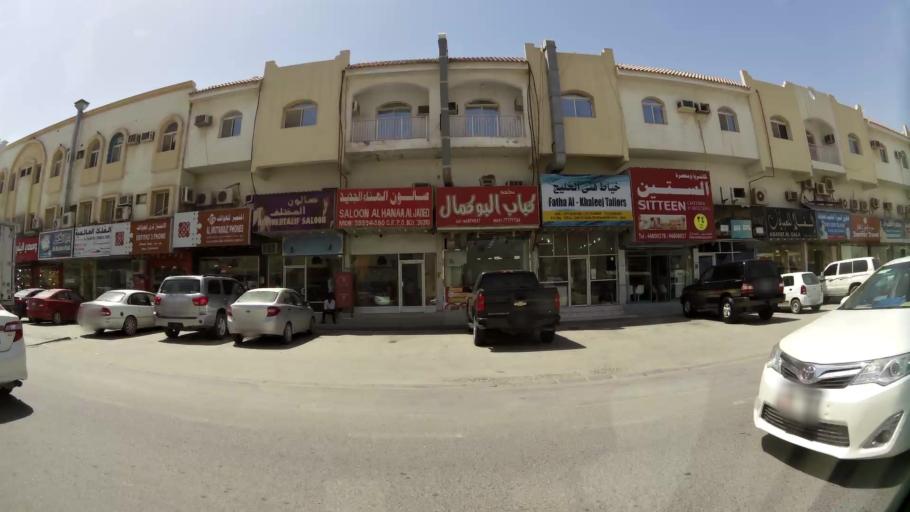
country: QA
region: Baladiyat ar Rayyan
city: Ar Rayyan
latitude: 25.2750
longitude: 51.4077
